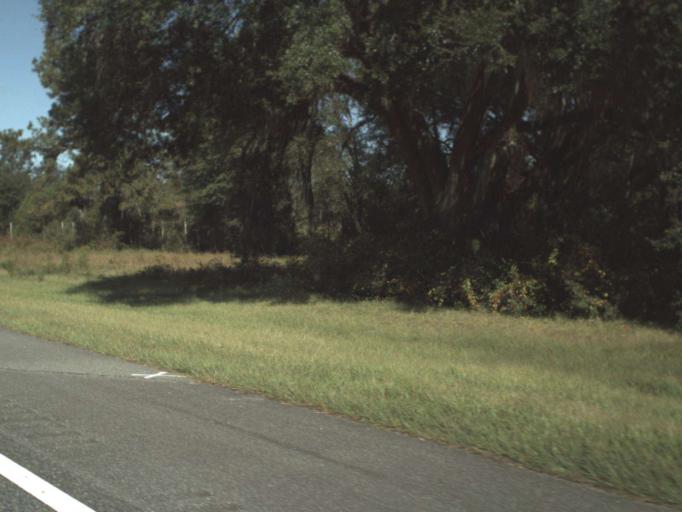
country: US
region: Florida
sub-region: Jackson County
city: Marianna
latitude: 30.7045
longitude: -85.1421
